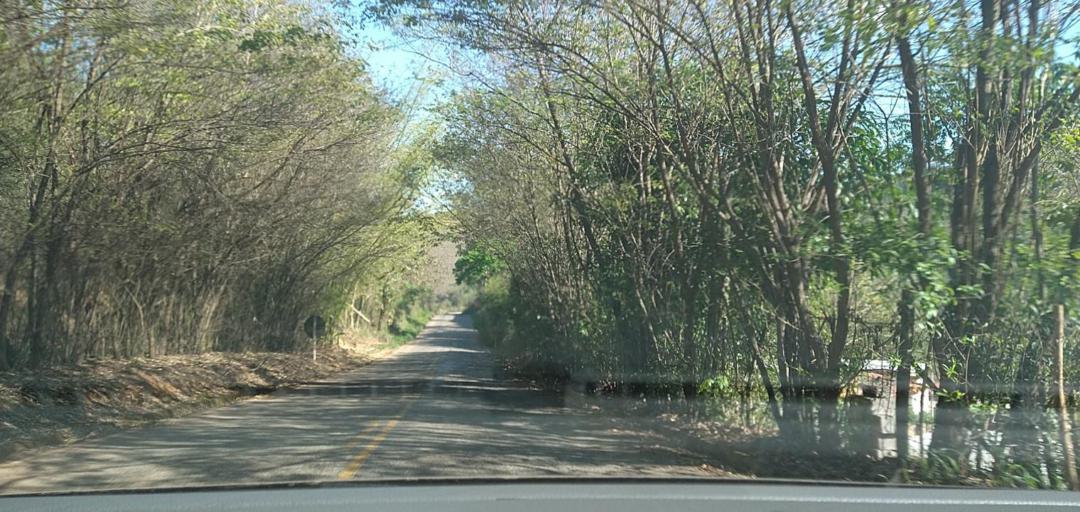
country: BR
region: Minas Gerais
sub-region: Ponte Nova
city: Ponte Nova
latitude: -20.2443
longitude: -42.8938
